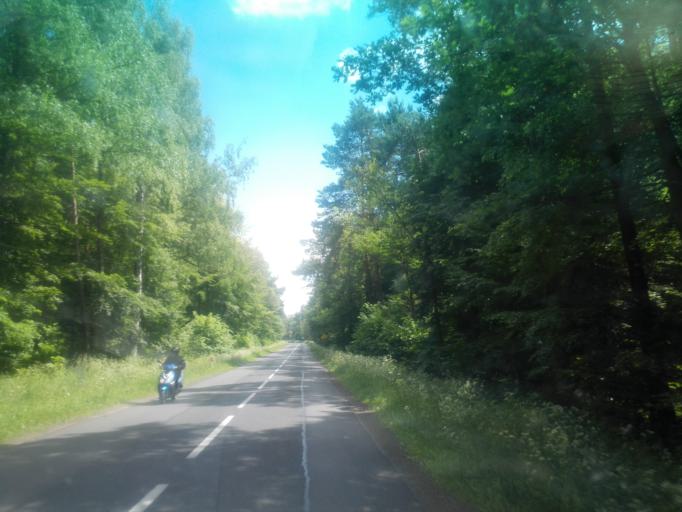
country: PL
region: Silesian Voivodeship
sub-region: Powiat czestochowski
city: Olsztyn
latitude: 50.7445
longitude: 19.3247
